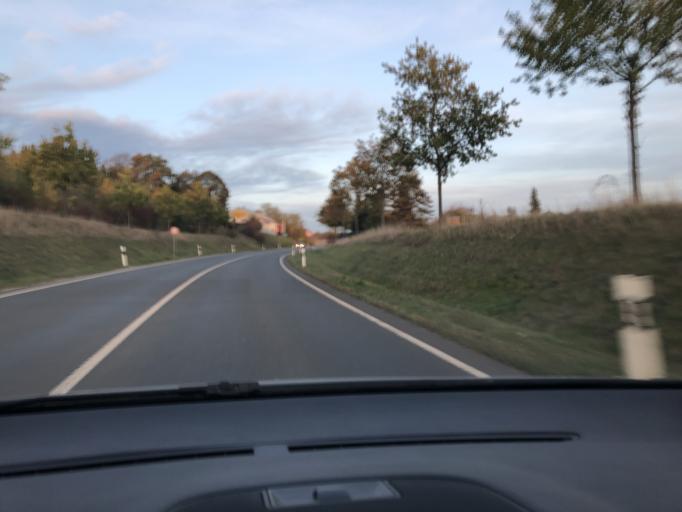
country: DE
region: Thuringia
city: Weimar
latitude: 50.9993
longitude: 11.2998
